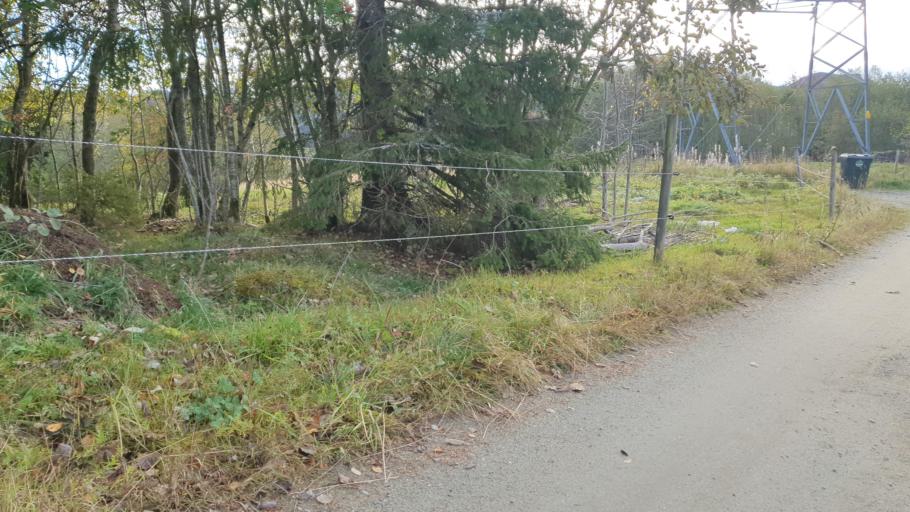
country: NO
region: Sor-Trondelag
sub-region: Klaebu
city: Klaebu
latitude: 63.2928
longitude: 10.4632
